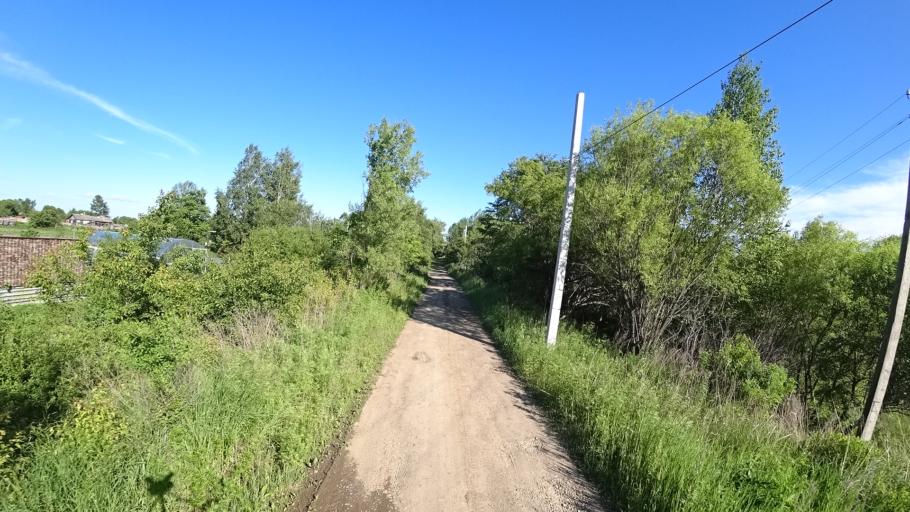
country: RU
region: Khabarovsk Krai
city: Khor
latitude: 47.8934
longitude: 134.9912
